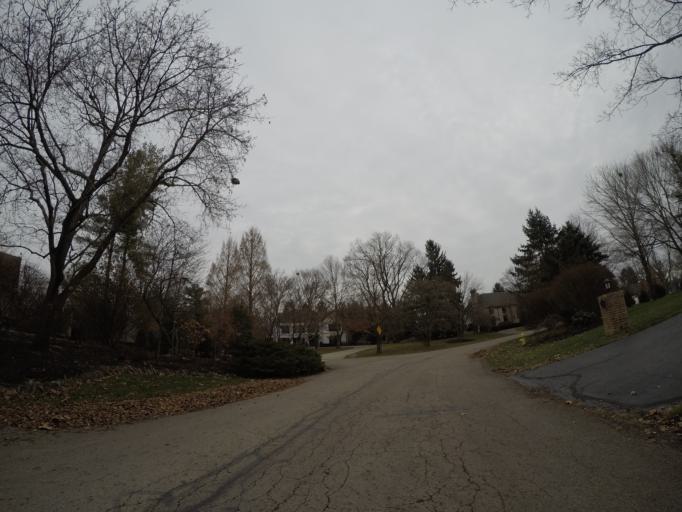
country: US
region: Ohio
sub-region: Franklin County
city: Dublin
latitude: 40.0523
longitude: -83.0881
